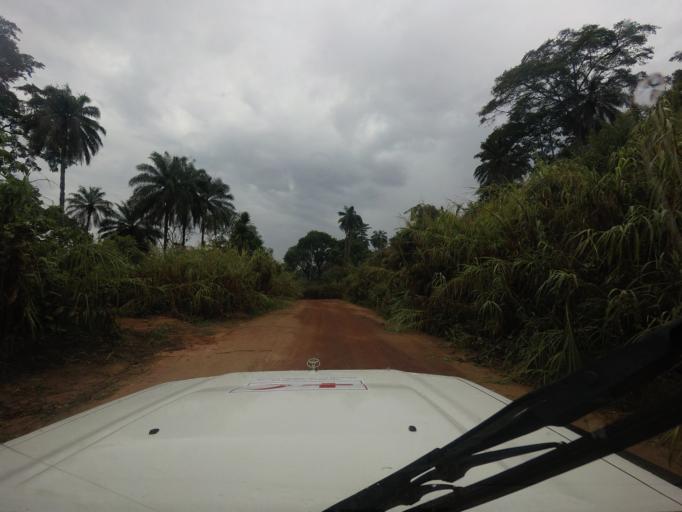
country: SL
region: Eastern Province
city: Buedu
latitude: 8.3475
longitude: -10.1801
